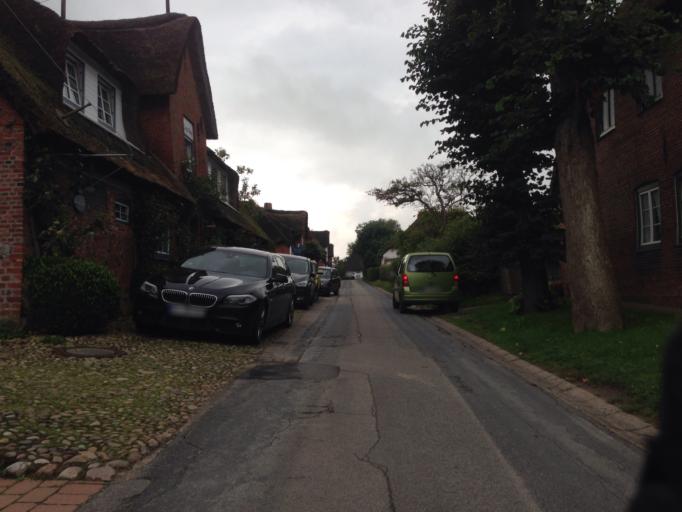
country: DE
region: Schleswig-Holstein
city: Oevenum
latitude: 54.7120
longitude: 8.5311
